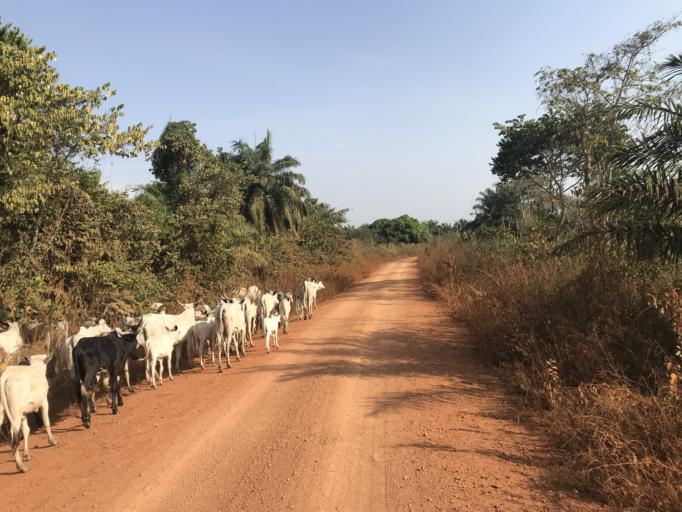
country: NG
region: Osun
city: Inisa
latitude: 7.7955
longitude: 4.2938
